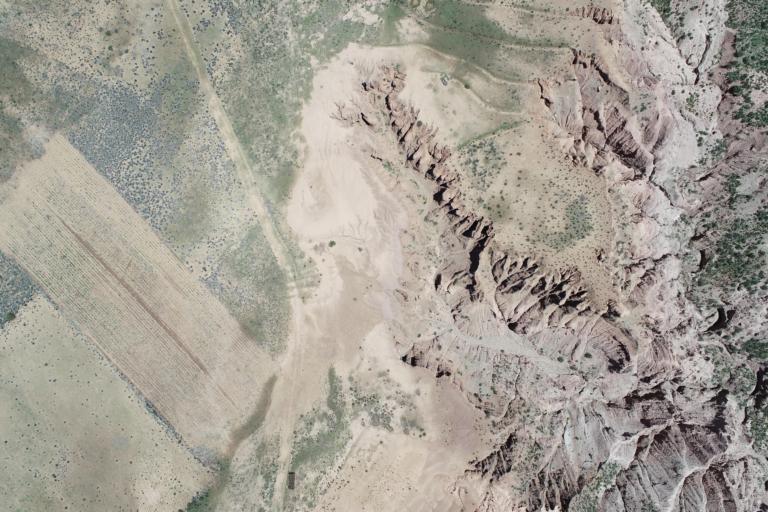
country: BO
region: La Paz
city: Curahuara de Carangas
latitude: -17.3112
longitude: -68.5073
